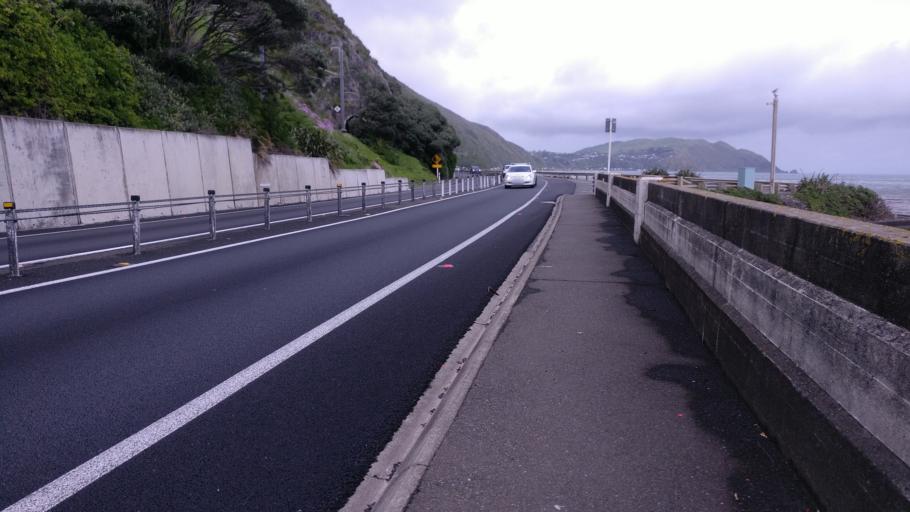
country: NZ
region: Wellington
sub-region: Kapiti Coast District
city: Paraparaumu
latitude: -41.0085
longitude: 174.9245
